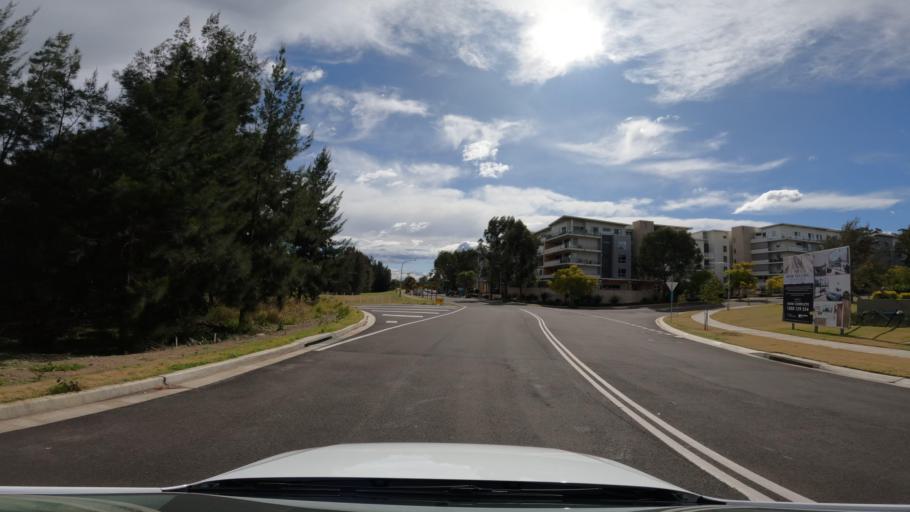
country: AU
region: New South Wales
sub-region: Blacktown
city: Stanhope Gardens
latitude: -33.7219
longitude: 150.9435
